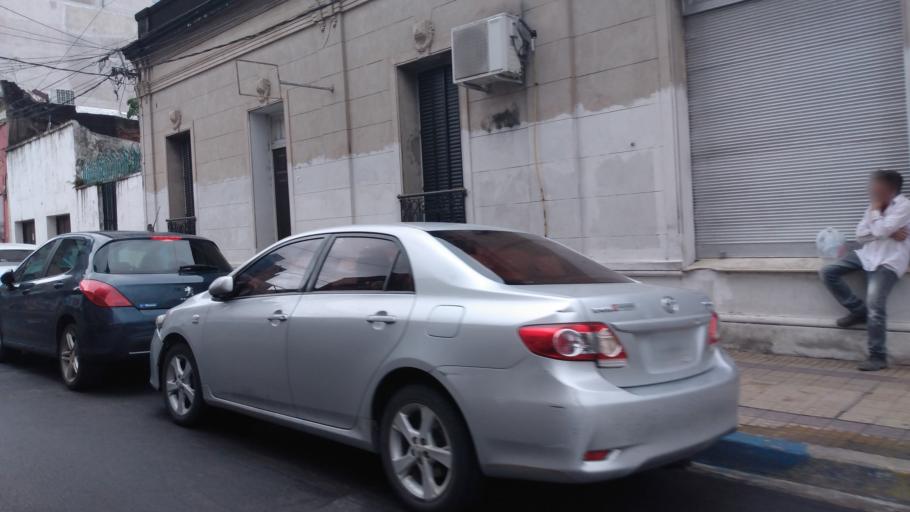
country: AR
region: Corrientes
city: Corrientes
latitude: -27.4689
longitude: -58.8332
